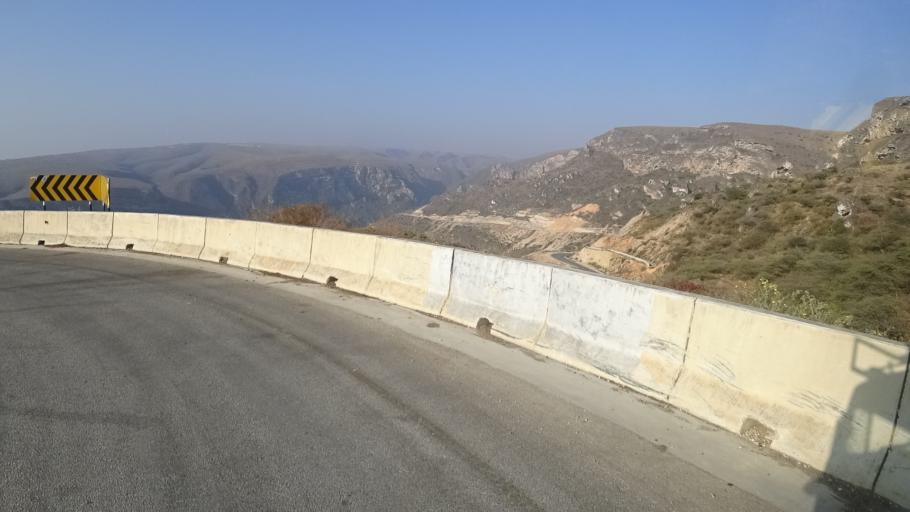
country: YE
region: Al Mahrah
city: Hawf
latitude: 16.7563
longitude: 53.2316
